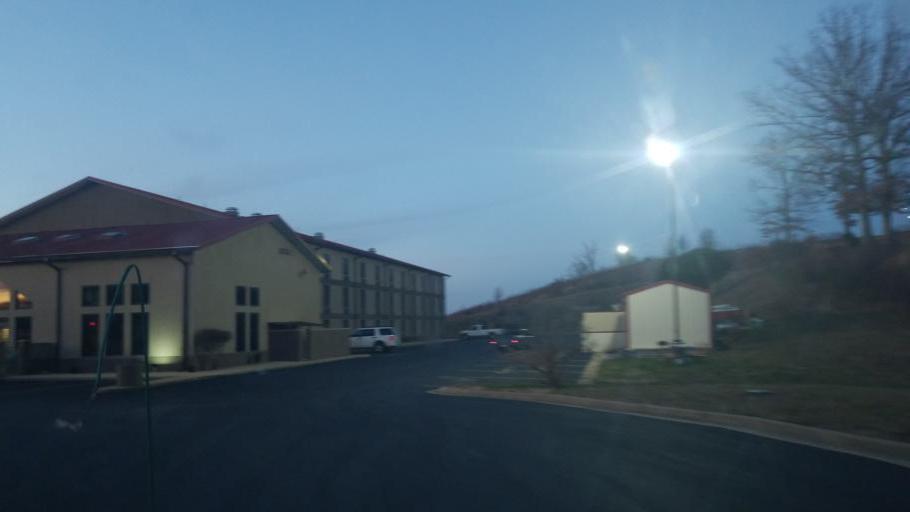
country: US
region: Missouri
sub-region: Howell County
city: West Plains
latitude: 36.7262
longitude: -91.8764
